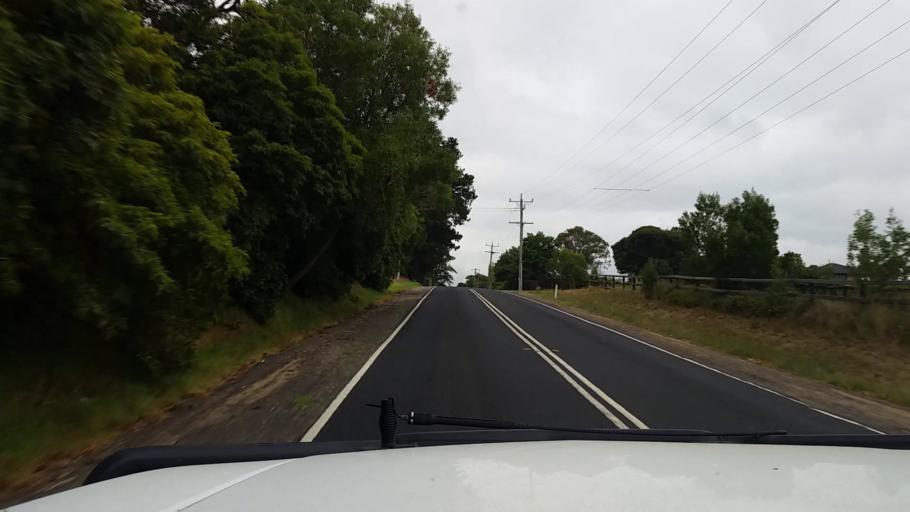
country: AU
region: Victoria
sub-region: Mornington Peninsula
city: Hastings
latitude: -38.2920
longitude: 145.1456
